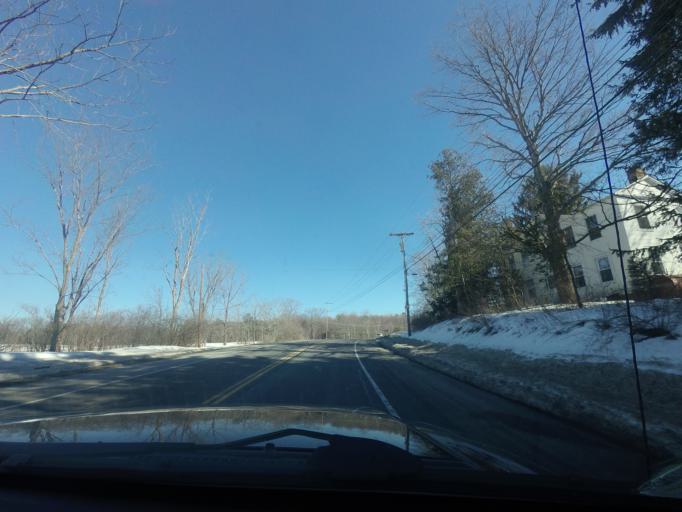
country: US
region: New York
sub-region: Rensselaer County
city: Nassau
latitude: 42.5281
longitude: -73.6480
